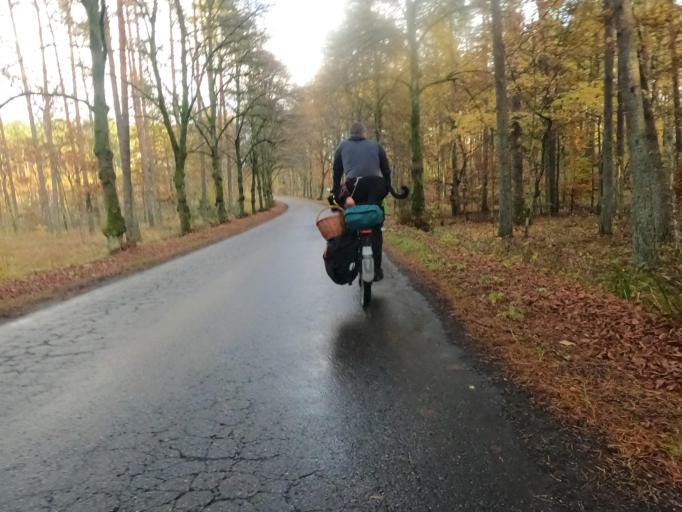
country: PL
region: West Pomeranian Voivodeship
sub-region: Powiat szczecinecki
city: Borne Sulinowo
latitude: 53.5298
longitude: 16.4850
